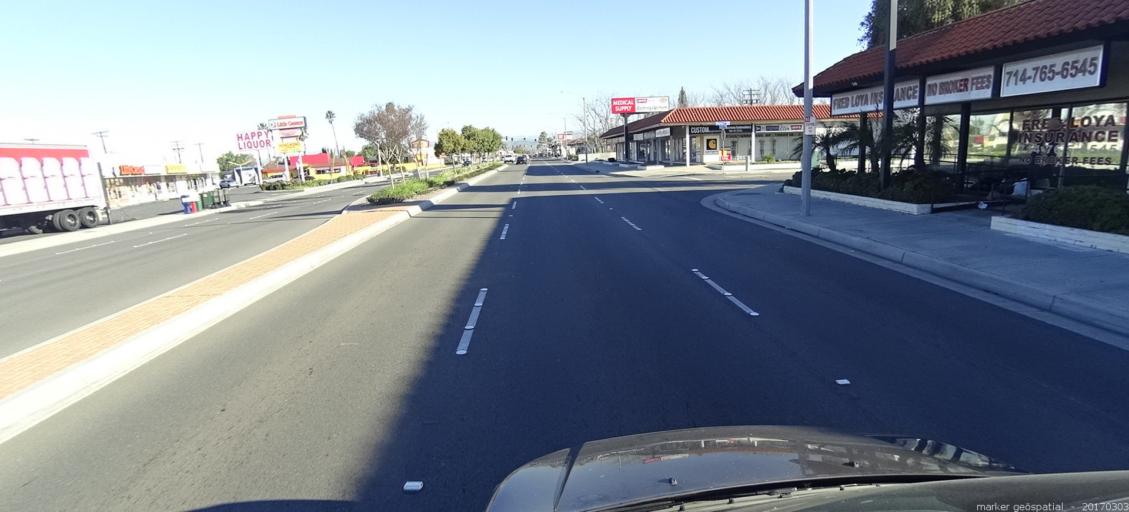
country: US
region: California
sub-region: Orange County
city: Anaheim
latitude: 33.8346
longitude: -117.8892
